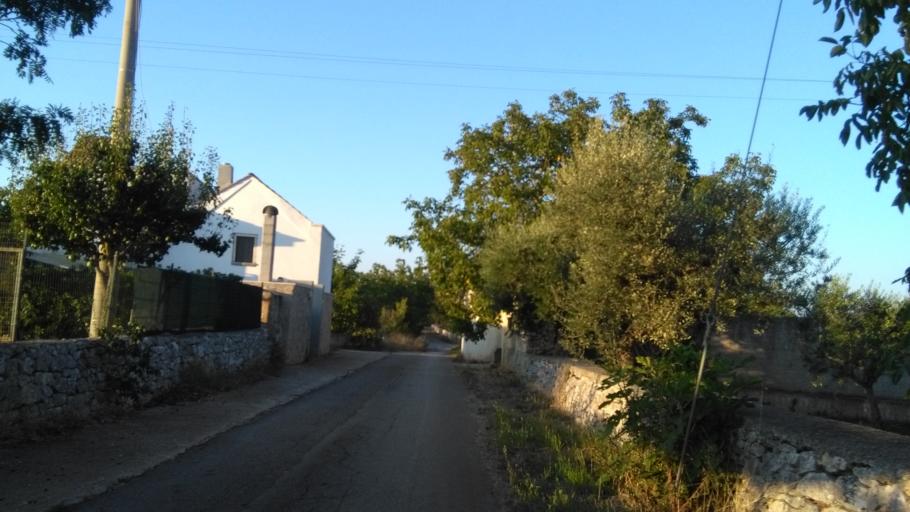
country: IT
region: Apulia
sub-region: Provincia di Bari
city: Putignano
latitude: 40.8254
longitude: 17.0920
